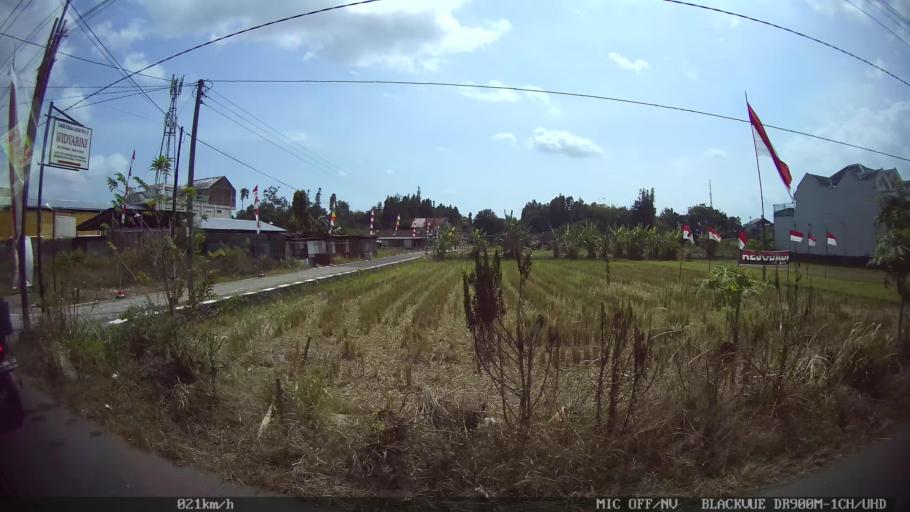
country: ID
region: Daerah Istimewa Yogyakarta
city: Gamping Lor
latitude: -7.8023
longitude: 110.3332
